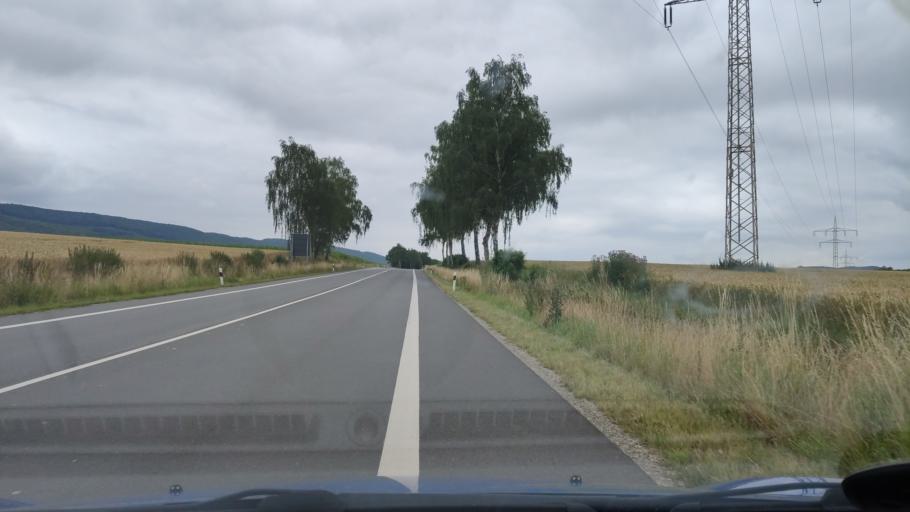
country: DE
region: Lower Saxony
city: Dielmissen
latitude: 51.9712
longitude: 9.5927
